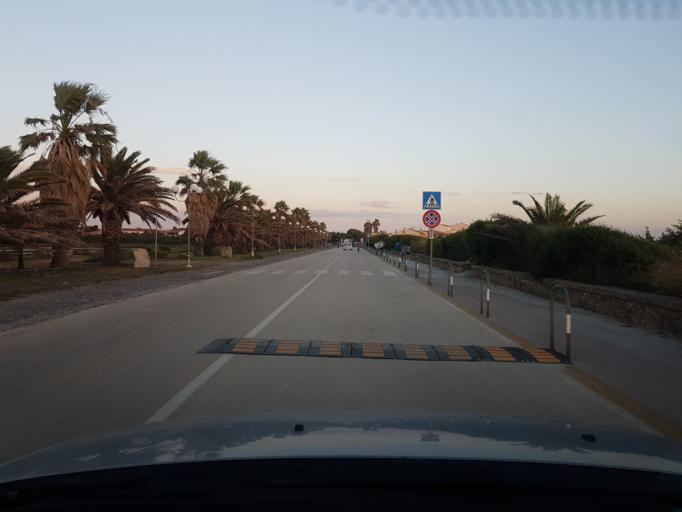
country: IT
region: Sardinia
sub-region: Provincia di Oristano
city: Riola Sardo
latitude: 40.0300
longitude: 8.4060
